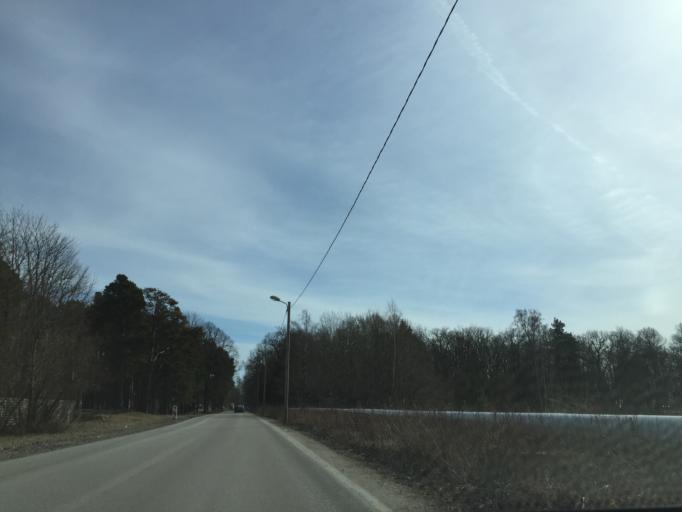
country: EE
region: Paernumaa
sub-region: Paernu linn
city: Parnu
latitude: 58.3796
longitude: 24.5337
